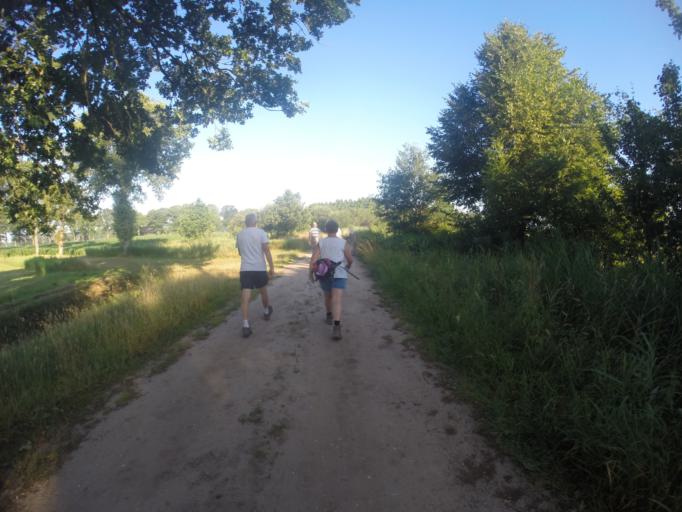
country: NL
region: Gelderland
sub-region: Gemeente Lochem
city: Lochem
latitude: 52.1216
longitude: 6.3975
